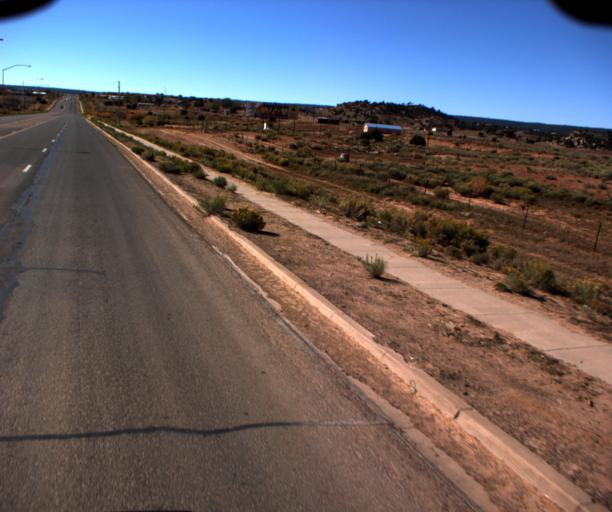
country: US
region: Arizona
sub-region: Apache County
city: Saint Michaels
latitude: 35.6591
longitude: -109.0804
